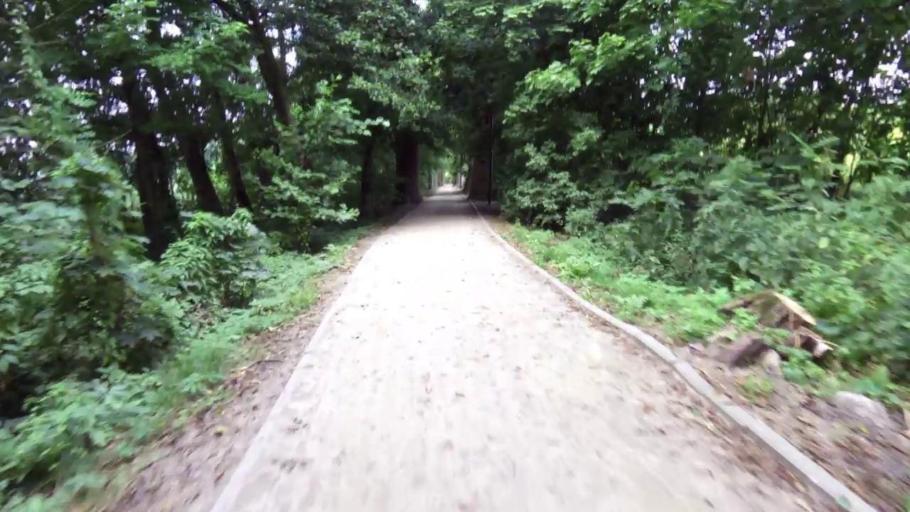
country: PL
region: West Pomeranian Voivodeship
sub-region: Powiat choszczenski
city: Choszczno
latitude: 53.1549
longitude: 15.4324
